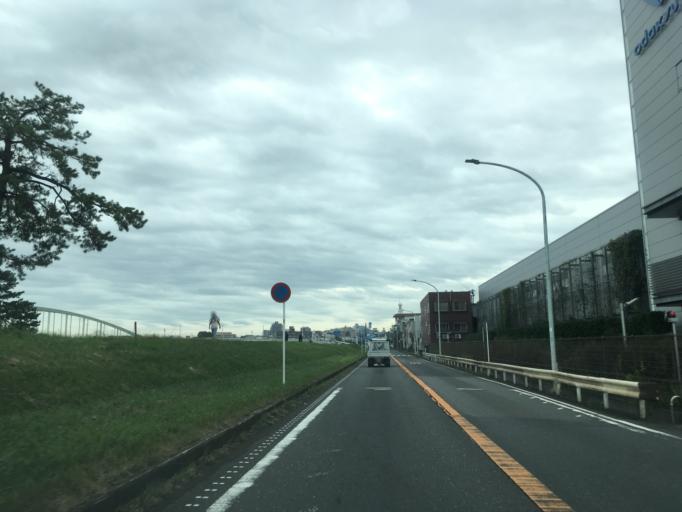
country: JP
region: Tokyo
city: Chofugaoka
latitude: 35.6273
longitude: 139.5651
